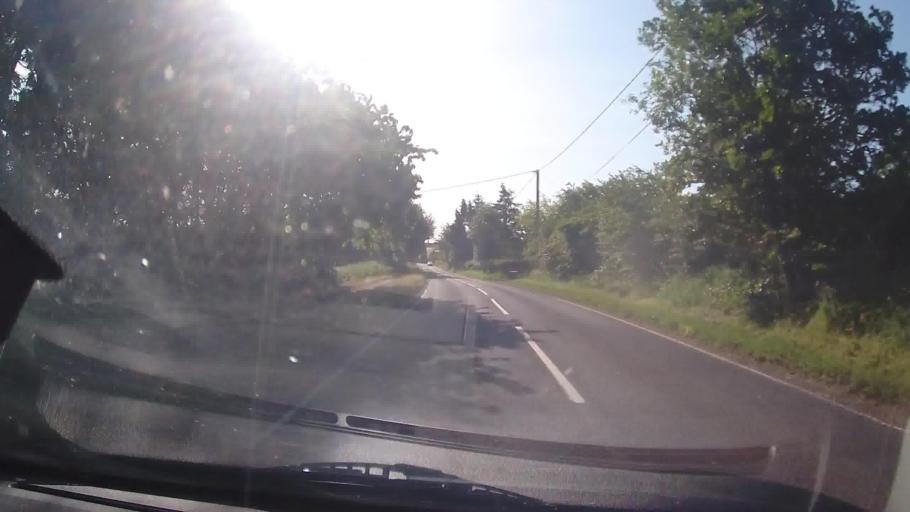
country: GB
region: England
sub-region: Shropshire
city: Withington
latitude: 52.7352
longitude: -2.5669
